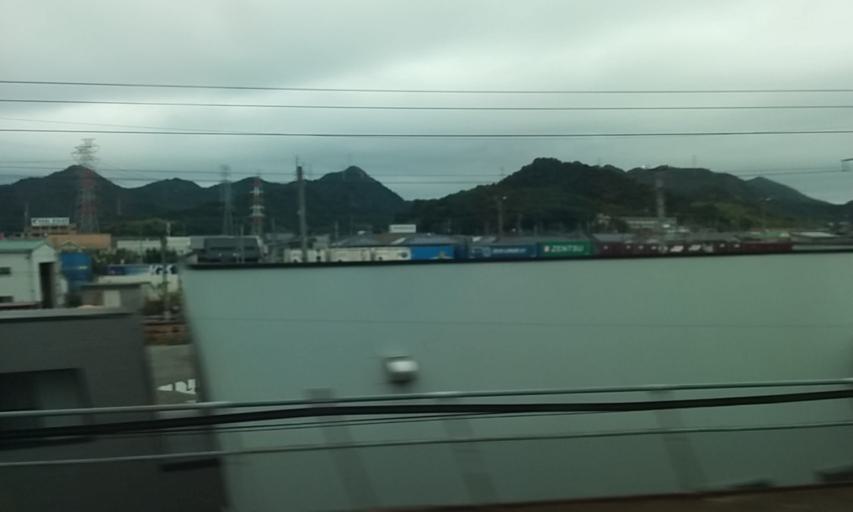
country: JP
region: Hyogo
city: Shirahamacho-usazakiminami
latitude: 34.8074
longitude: 134.7480
